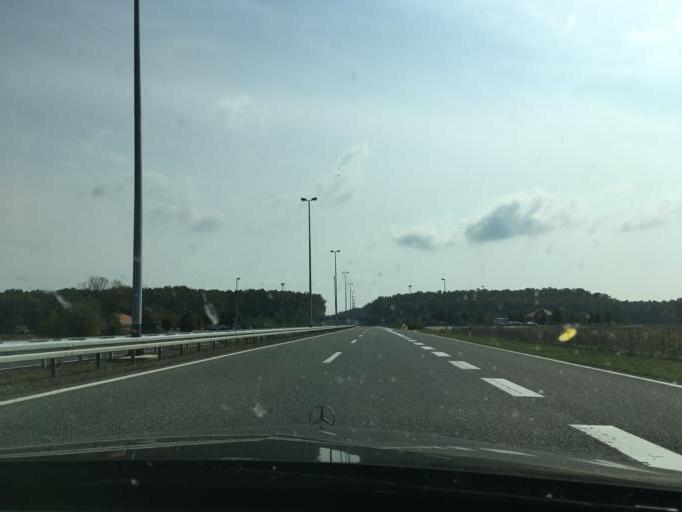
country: HR
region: Vukovarsko-Srijemska
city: Bosnjaci
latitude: 45.0582
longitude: 18.8102
